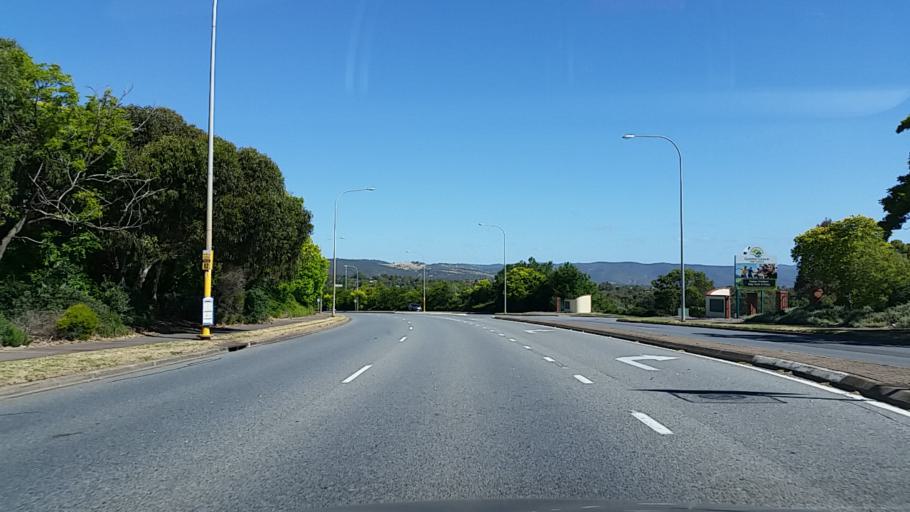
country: AU
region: South Australia
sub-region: Tea Tree Gully
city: Golden Grove
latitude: -34.7935
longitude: 138.6984
